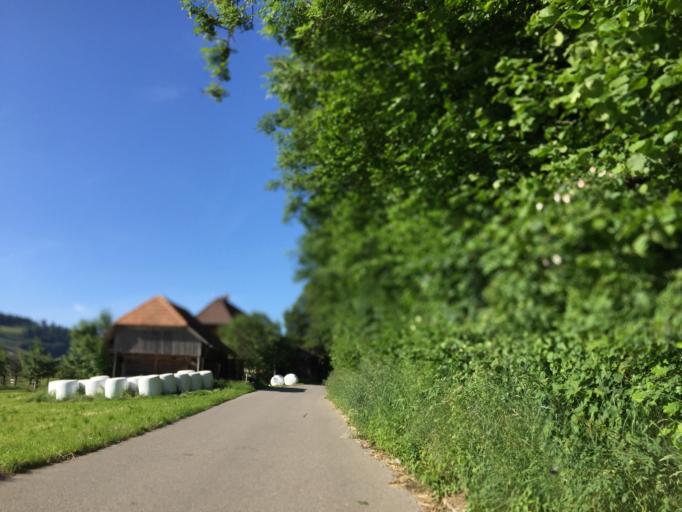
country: CH
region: Bern
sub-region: Bern-Mittelland District
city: Konolfingen
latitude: 46.8755
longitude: 7.6325
